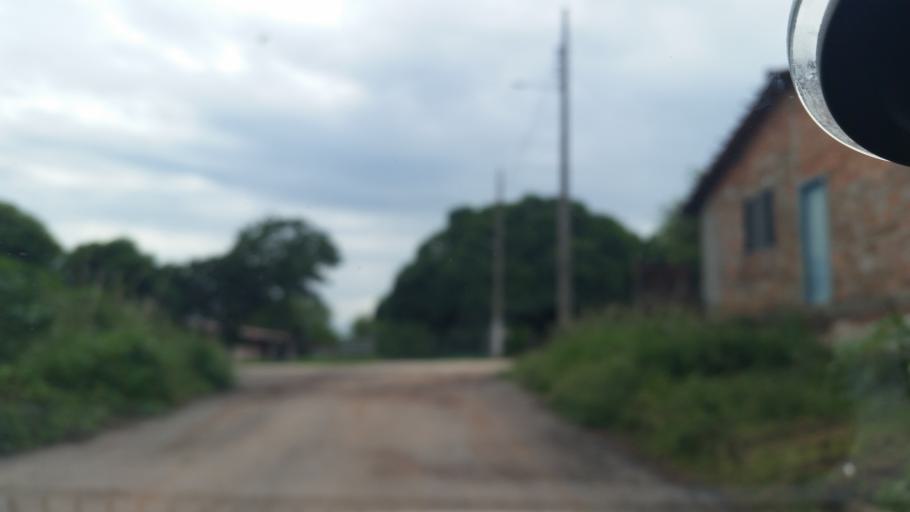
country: BR
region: Goias
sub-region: Uruacu
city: Uruacu
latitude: -14.0176
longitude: -49.1684
